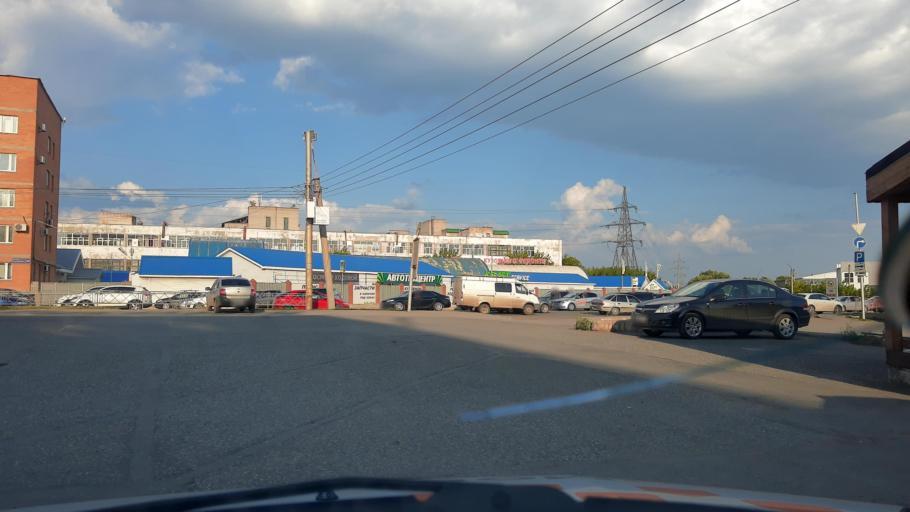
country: RU
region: Bashkortostan
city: Ufa
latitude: 54.7965
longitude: 56.0756
